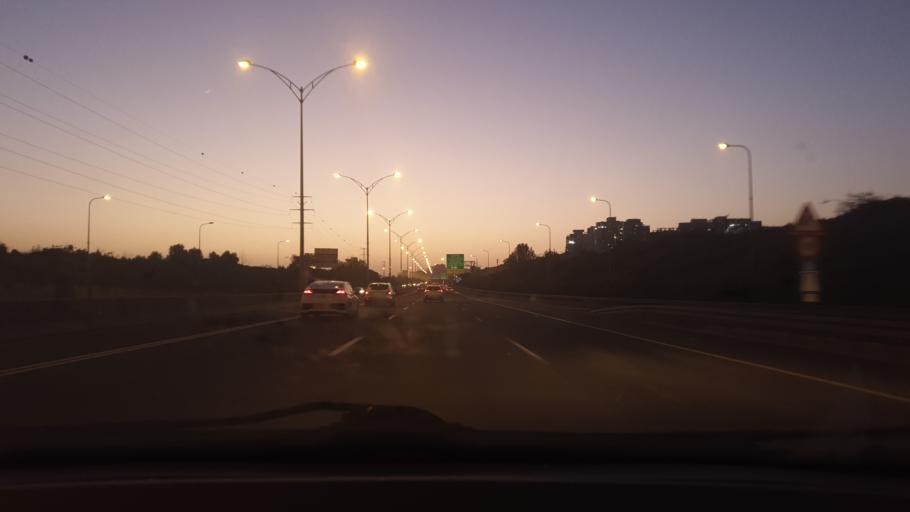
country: IL
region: Central District
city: Nehalim
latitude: 32.0676
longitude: 34.9173
